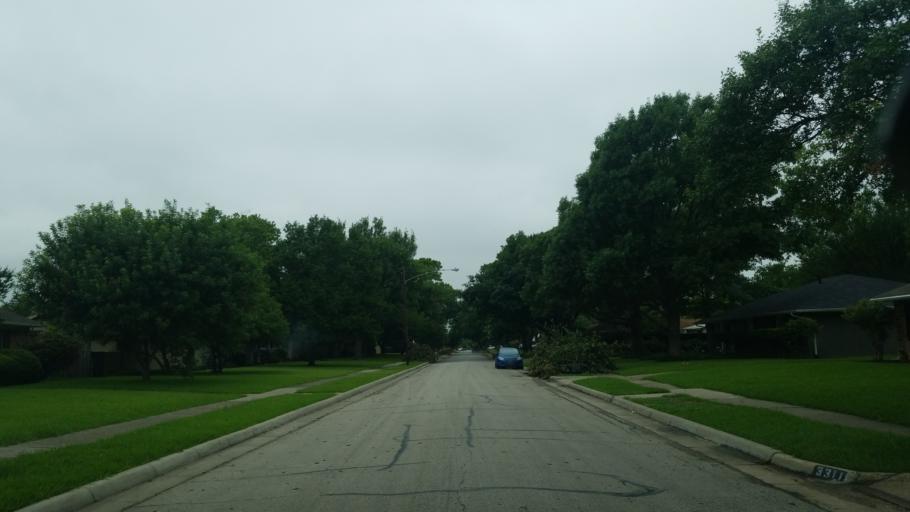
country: US
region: Texas
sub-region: Dallas County
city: Farmers Branch
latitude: 32.8987
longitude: -96.8676
